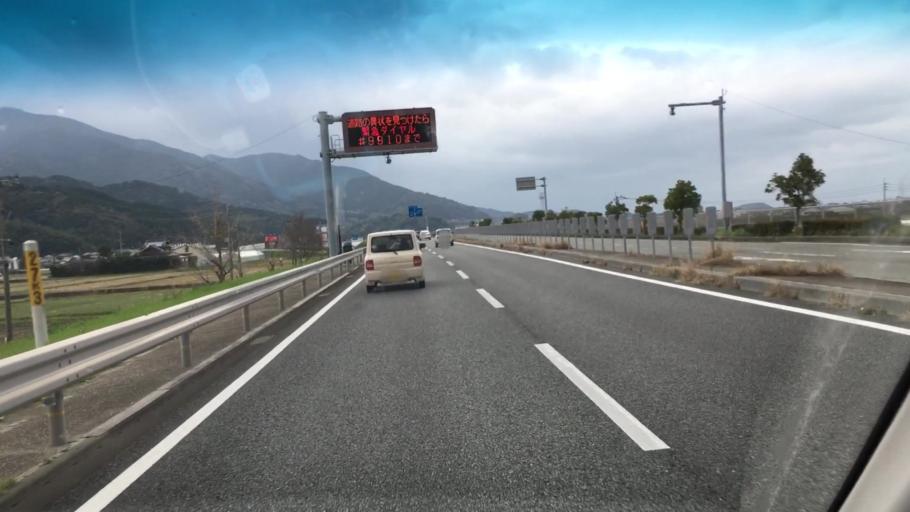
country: JP
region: Fukuoka
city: Maebaru-chuo
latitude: 33.5192
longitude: 130.1600
